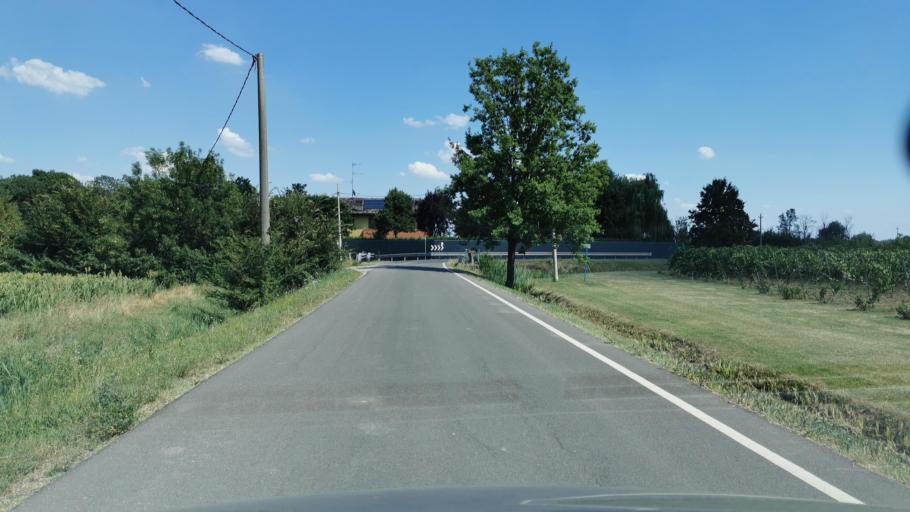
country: IT
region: Emilia-Romagna
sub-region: Provincia di Modena
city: Limidi
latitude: 44.7818
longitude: 10.9182
